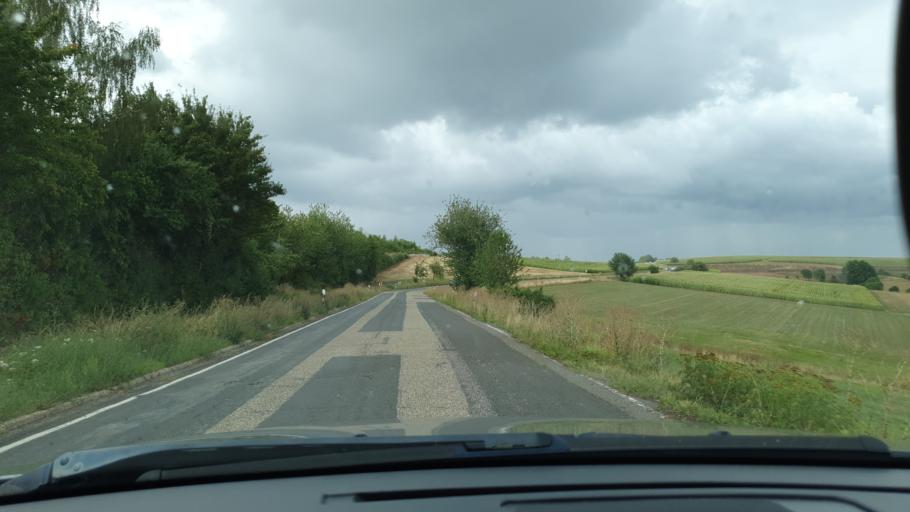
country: DE
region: Rheinland-Pfalz
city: Obernheim-Kirchenarnbach
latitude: 49.3571
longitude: 7.6050
